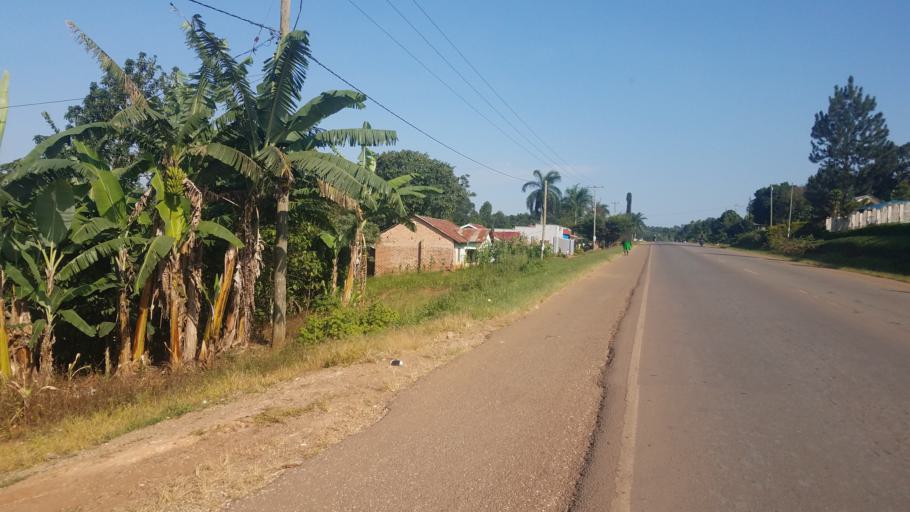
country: UG
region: Central Region
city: Masaka
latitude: -0.3383
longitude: 31.7009
